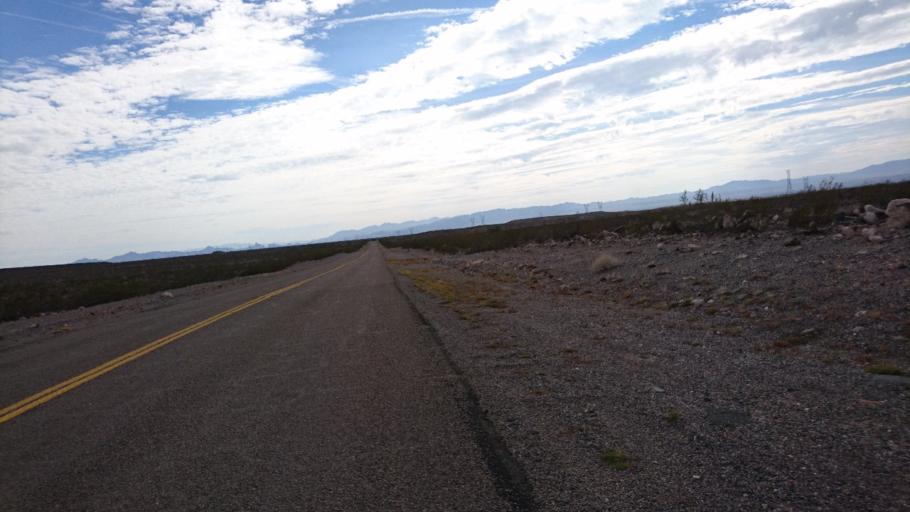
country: US
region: Arizona
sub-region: Mohave County
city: Mohave Valley
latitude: 34.8845
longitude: -114.4346
